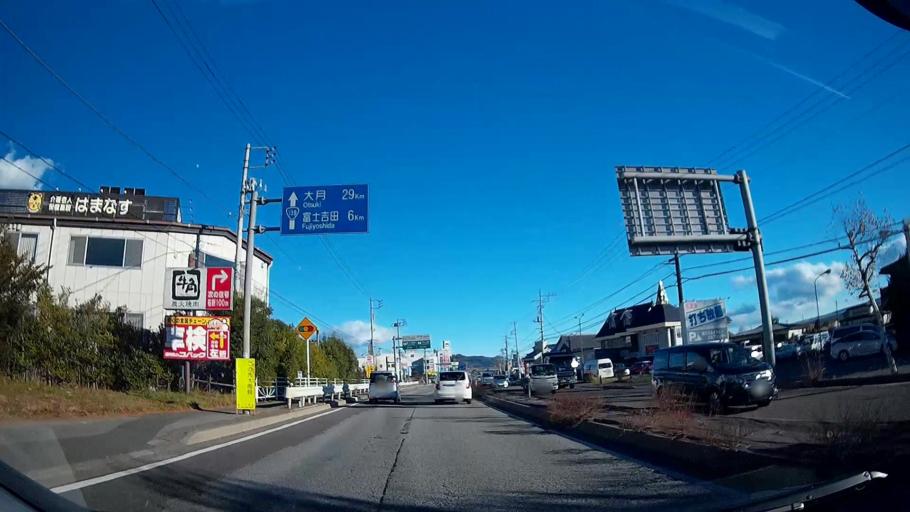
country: JP
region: Yamanashi
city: Fujikawaguchiko
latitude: 35.4911
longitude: 138.7602
